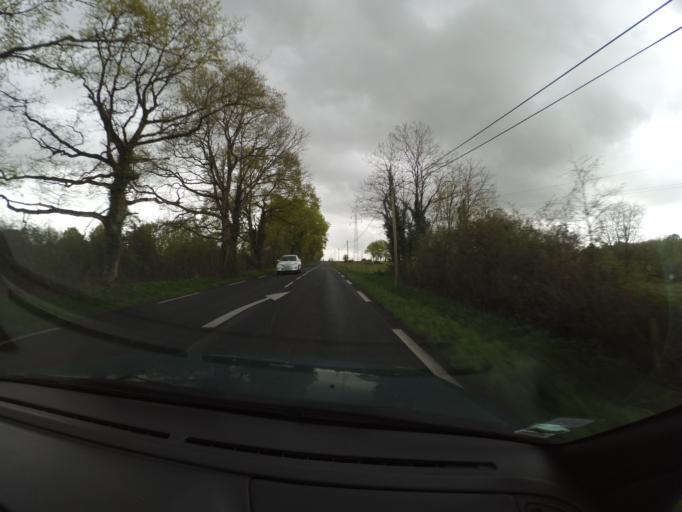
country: FR
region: Pays de la Loire
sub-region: Departement de la Loire-Atlantique
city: La Remaudiere
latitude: 47.1987
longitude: -1.2473
